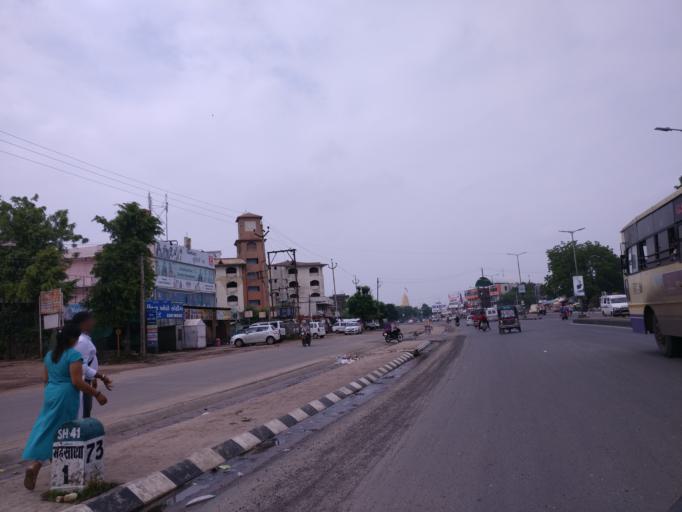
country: IN
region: Gujarat
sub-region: Mahesana
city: Visnagar
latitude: 23.5883
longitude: 72.3769
